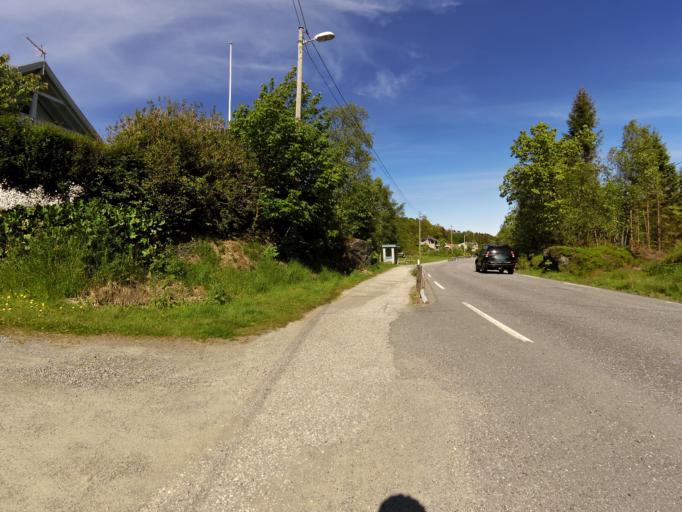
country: NO
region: Hordaland
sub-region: Stord
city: Sagvag
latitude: 59.7813
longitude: 5.3979
